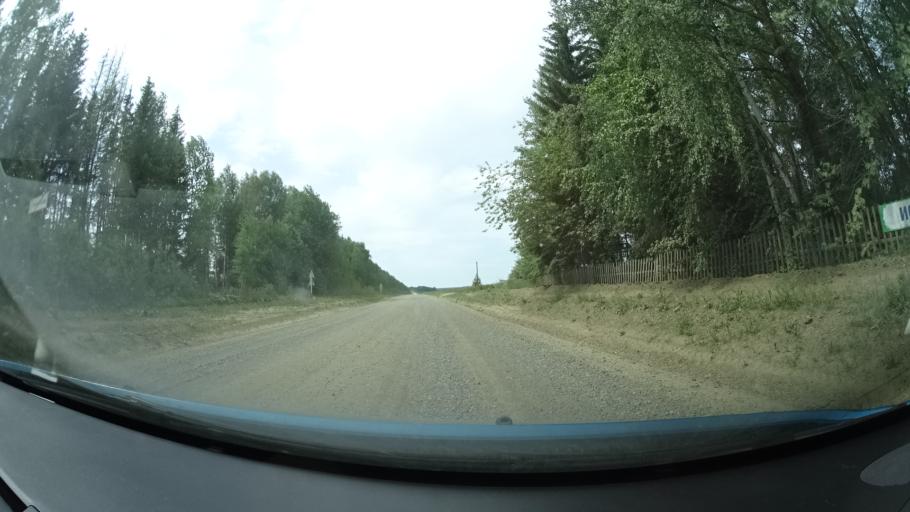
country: RU
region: Perm
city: Barda
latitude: 56.8104
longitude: 55.6577
